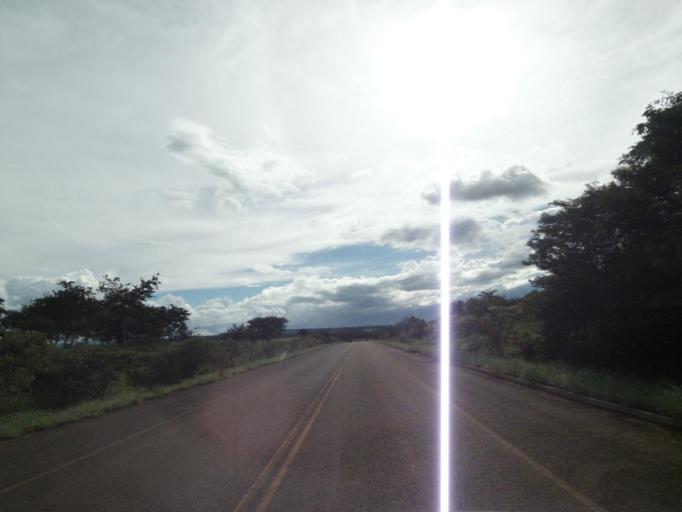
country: BR
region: Goias
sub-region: Jaragua
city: Jaragua
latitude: -15.8678
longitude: -49.4060
